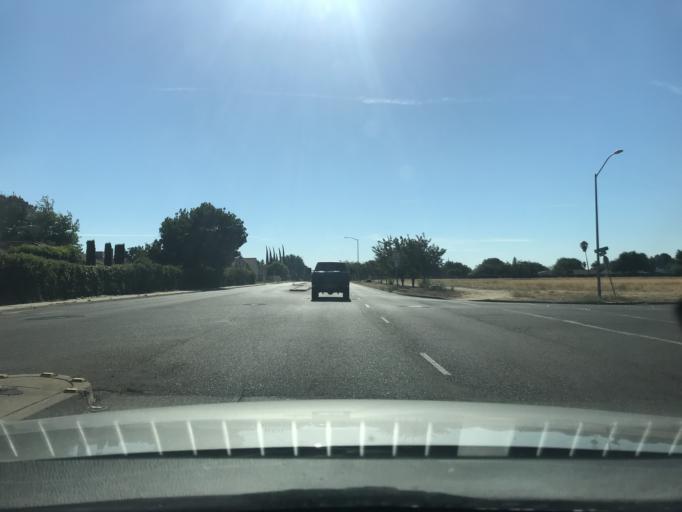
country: US
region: California
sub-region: Merced County
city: Atwater
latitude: 37.3498
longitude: -120.5851
